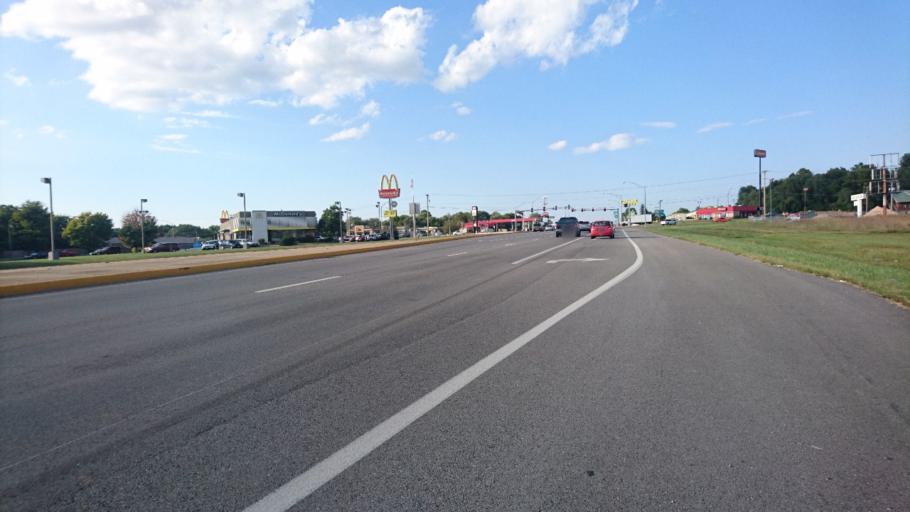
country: US
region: Missouri
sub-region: Greene County
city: Springfield
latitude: 37.2105
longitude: -93.3487
